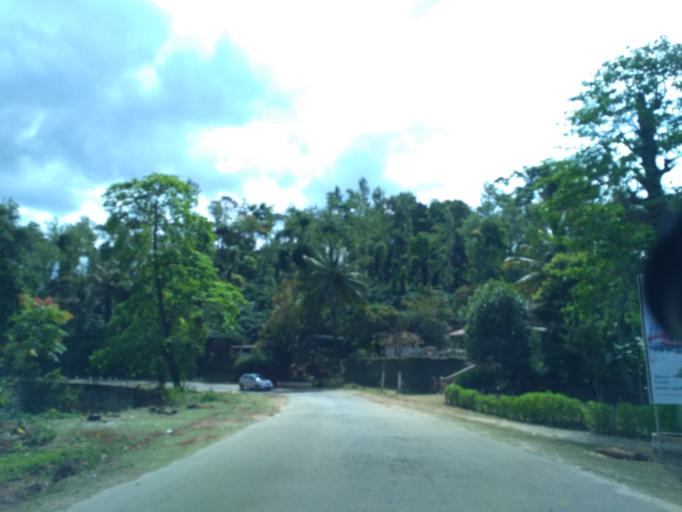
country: IN
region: Karnataka
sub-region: Kodagu
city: Madikeri
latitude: 12.3800
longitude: 75.7070
